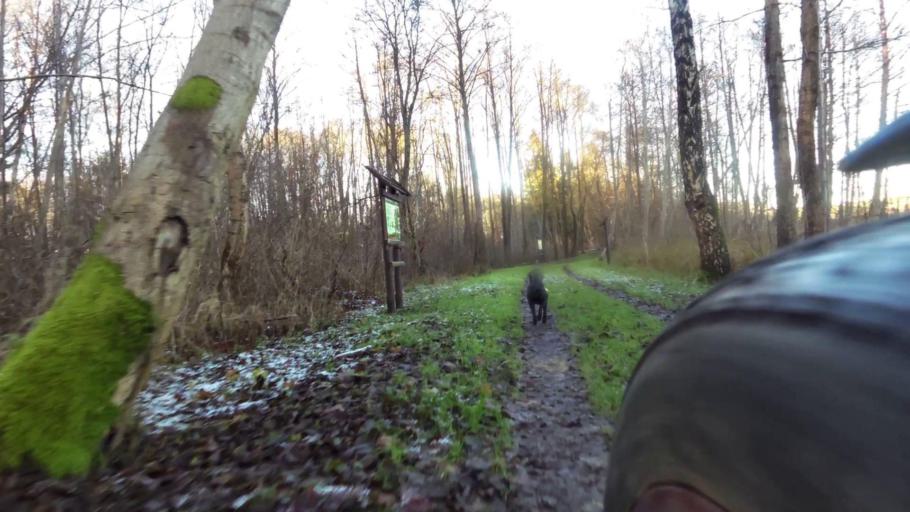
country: PL
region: West Pomeranian Voivodeship
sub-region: Powiat szczecinecki
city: Borne Sulinowo
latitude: 53.5910
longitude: 16.5362
